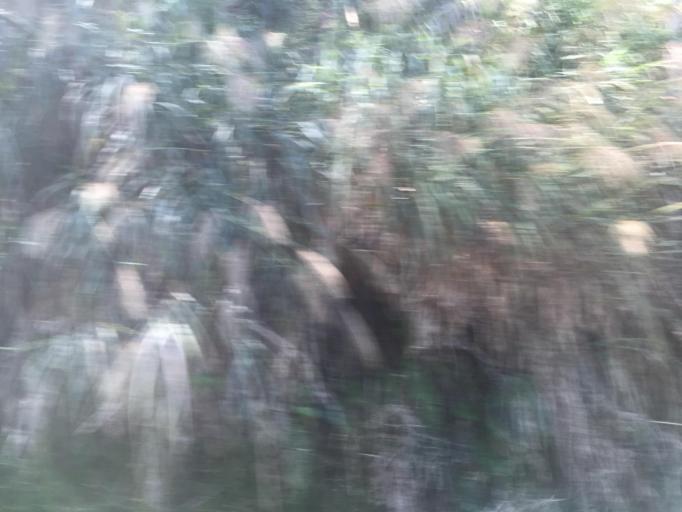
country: TW
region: Taiwan
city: Daxi
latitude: 24.5734
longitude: 121.4184
